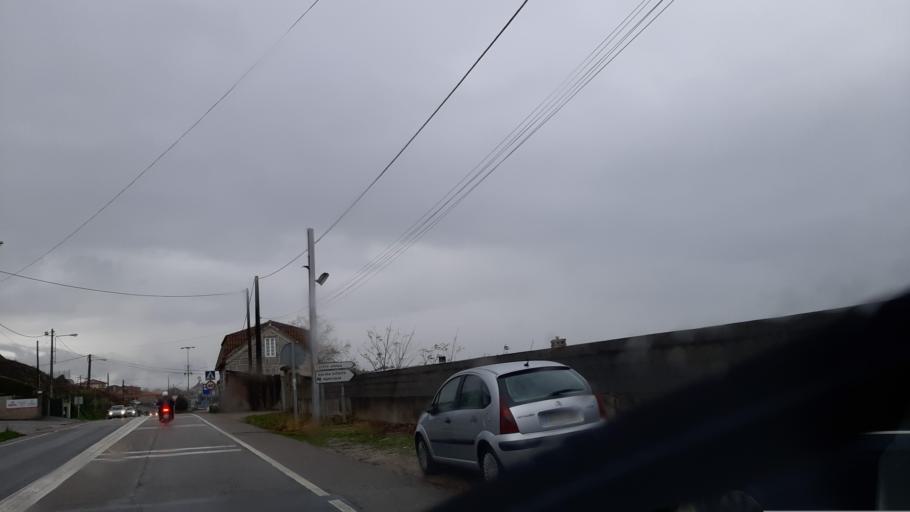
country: ES
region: Galicia
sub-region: Provincia de Pontevedra
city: Nigran
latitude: 42.1682
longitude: -8.8012
